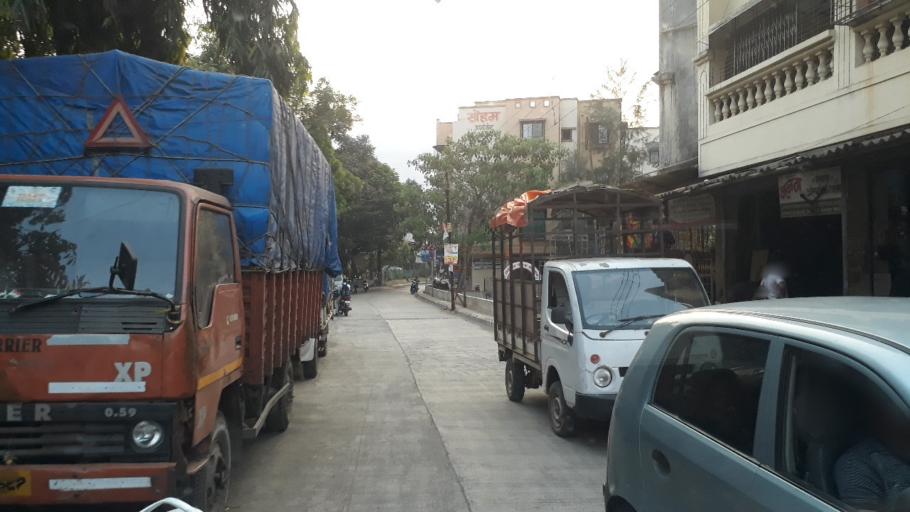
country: IN
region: Maharashtra
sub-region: Raigarh
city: Neral
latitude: 19.0232
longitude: 73.3161
